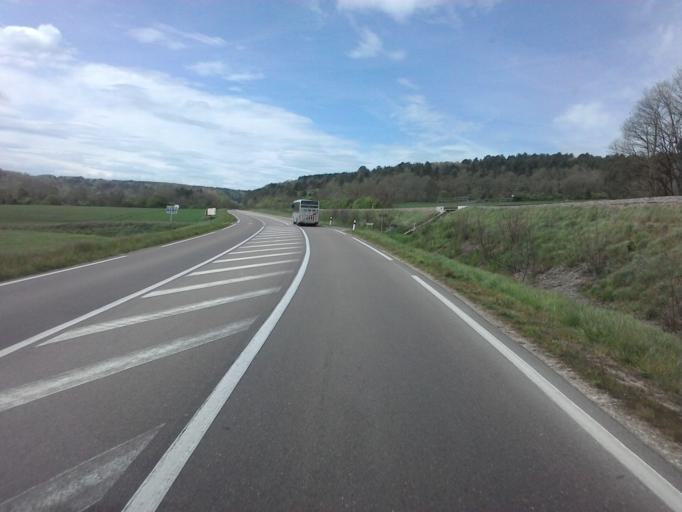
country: FR
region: Bourgogne
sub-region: Departement de l'Yonne
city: Vermenton
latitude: 47.6139
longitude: 3.7563
